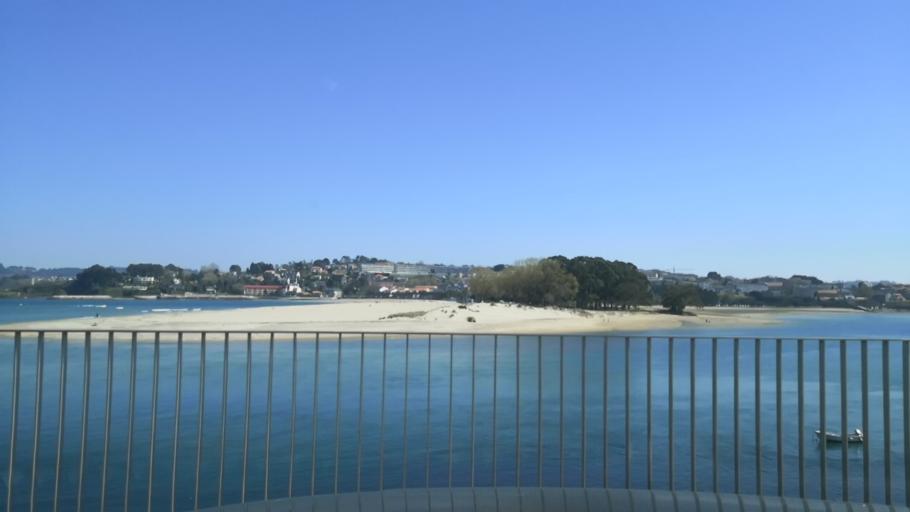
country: ES
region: Galicia
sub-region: Provincia da Coruna
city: A Coruna
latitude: 43.3416
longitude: -8.3873
